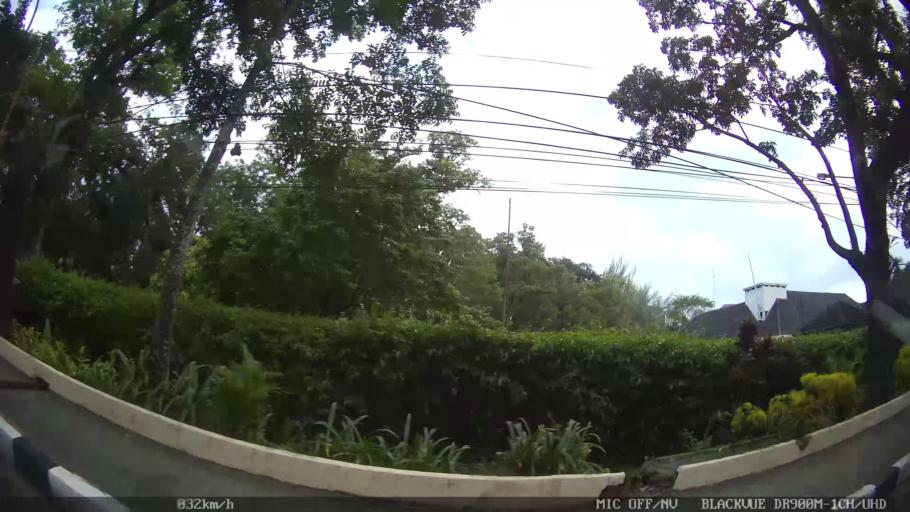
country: ID
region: North Sumatra
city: Medan
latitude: 3.5769
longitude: 98.6763
